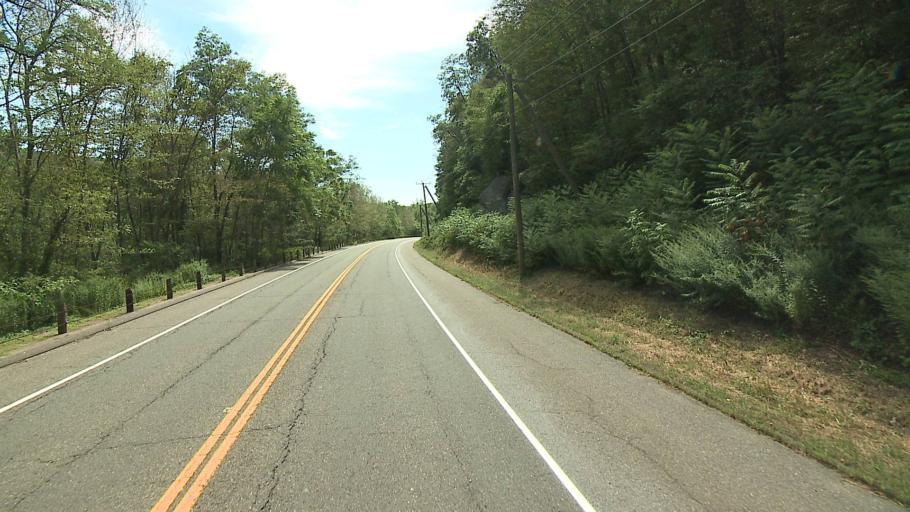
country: US
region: Connecticut
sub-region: Hartford County
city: Collinsville
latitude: 41.7980
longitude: -72.9265
